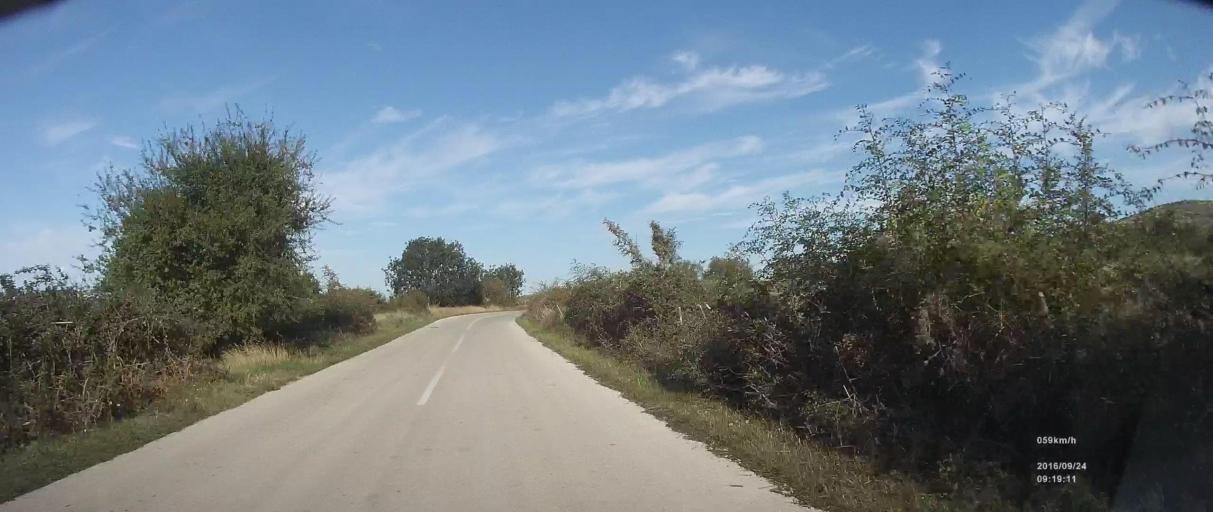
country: HR
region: Zadarska
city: Polaca
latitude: 44.0604
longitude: 15.5061
